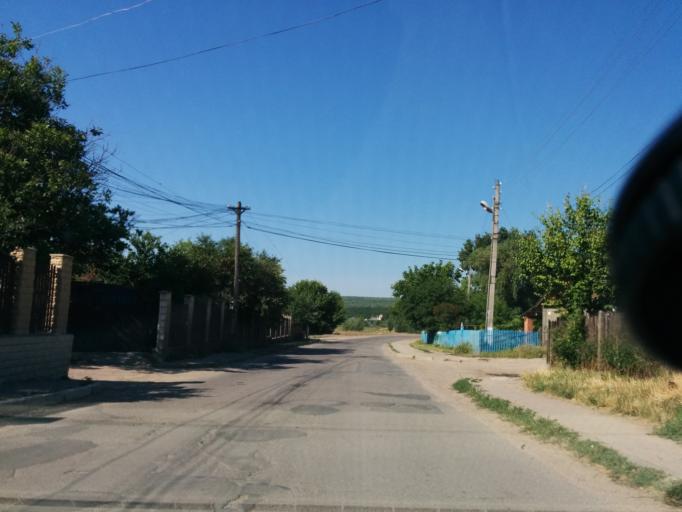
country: MD
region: Chisinau
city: Vadul lui Voda
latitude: 47.0630
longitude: 29.0070
